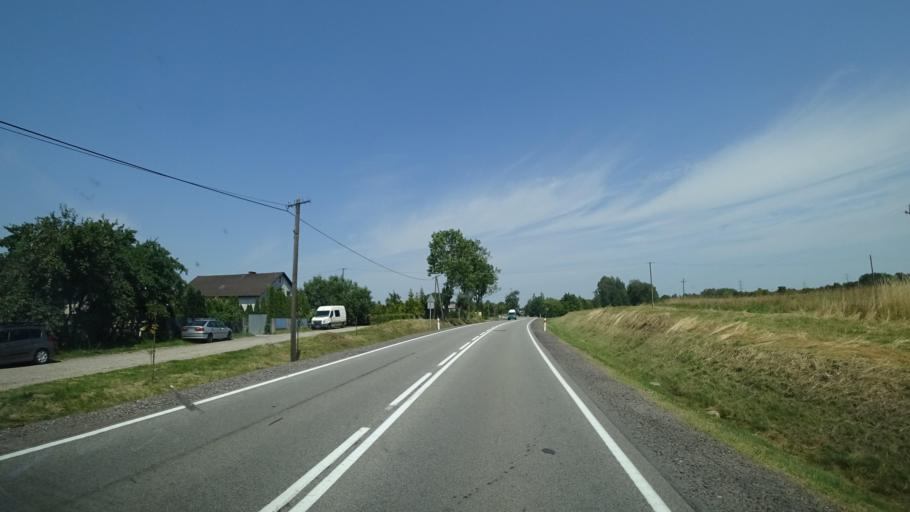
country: PL
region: Pomeranian Voivodeship
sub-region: Powiat koscierski
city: Koscierzyna
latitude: 54.1472
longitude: 18.0264
